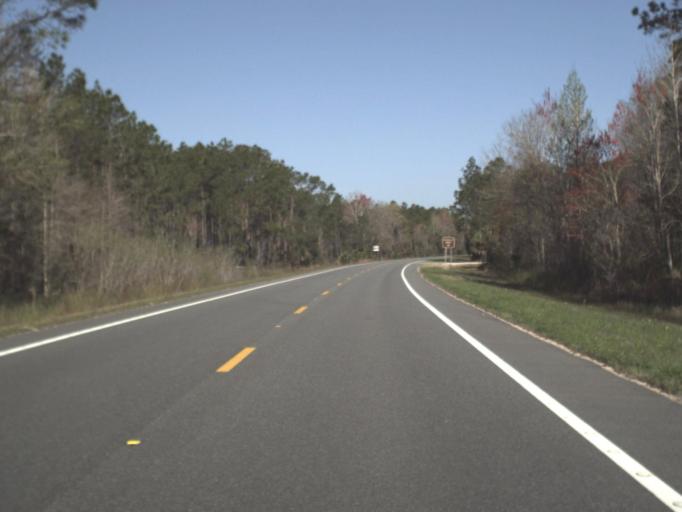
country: US
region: Florida
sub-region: Leon County
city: Woodville
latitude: 30.1616
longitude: -84.0026
